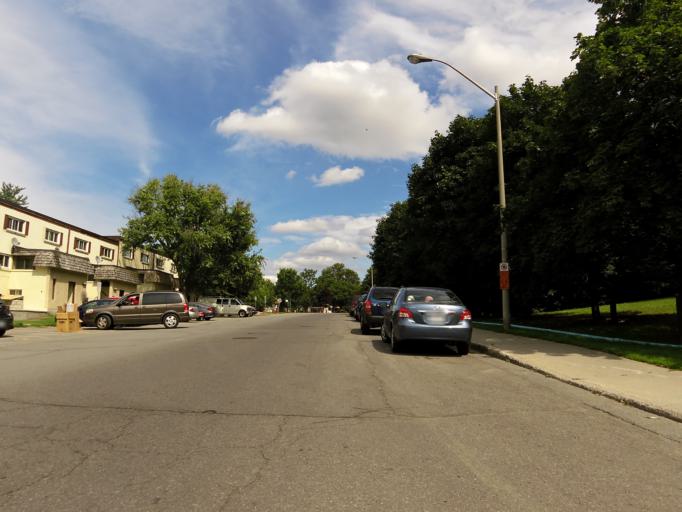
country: CA
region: Ontario
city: Ottawa
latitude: 45.4460
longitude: -75.6477
